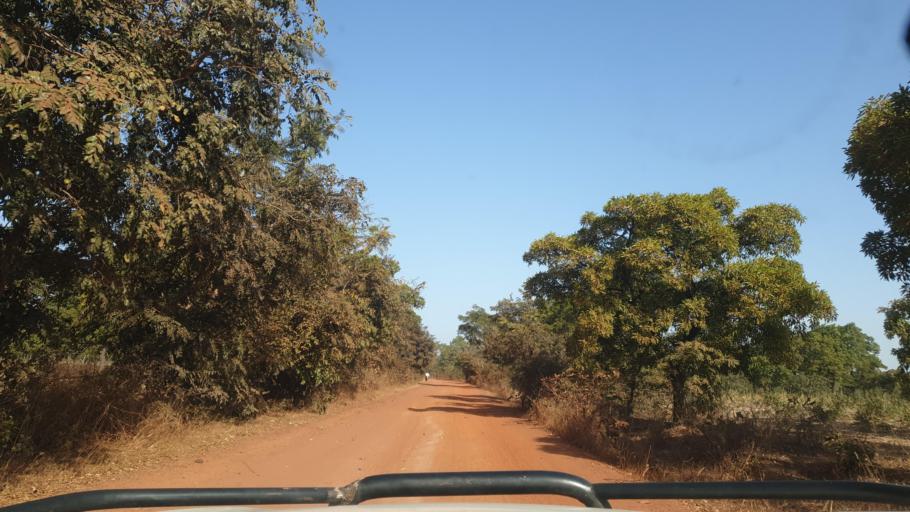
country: ML
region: Sikasso
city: Kolondieba
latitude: 11.7421
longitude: -6.8955
